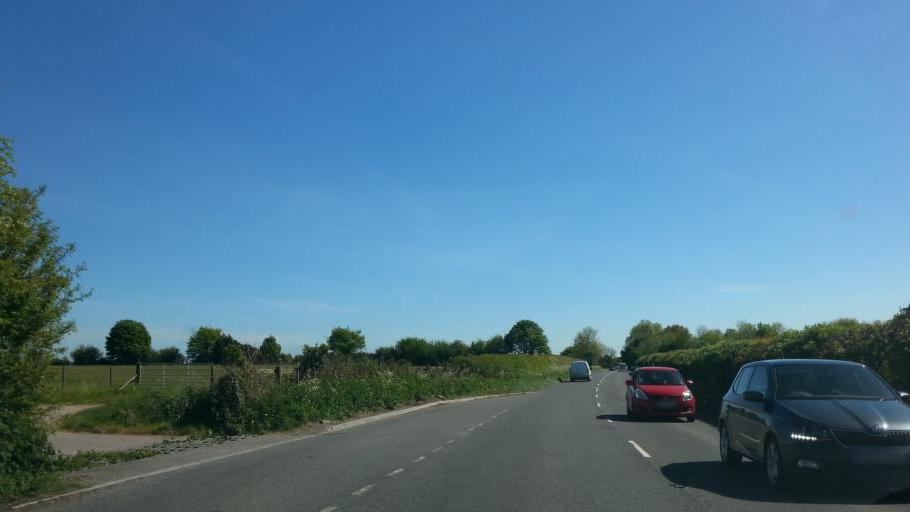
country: GB
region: England
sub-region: Dorset
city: Shaftesbury
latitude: 51.0236
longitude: -2.1886
